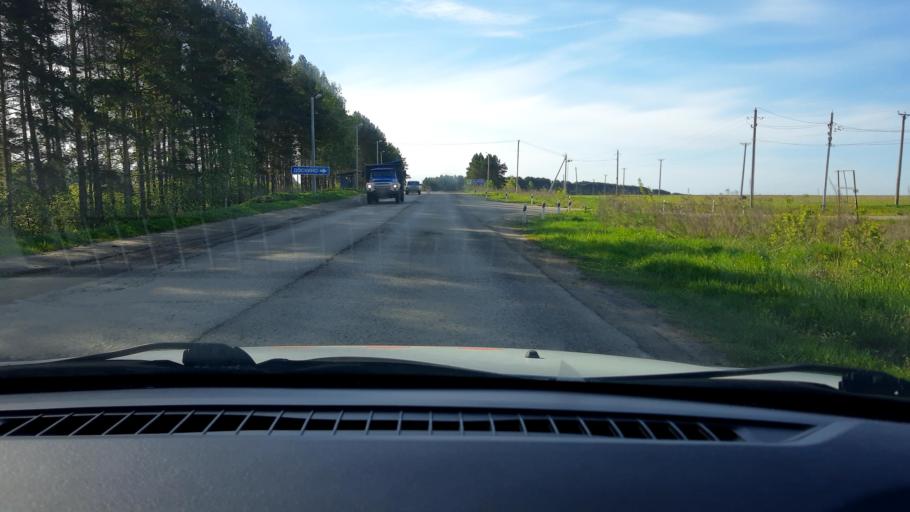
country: RU
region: Nizjnij Novgorod
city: Burevestnik
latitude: 56.1640
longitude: 43.7711
